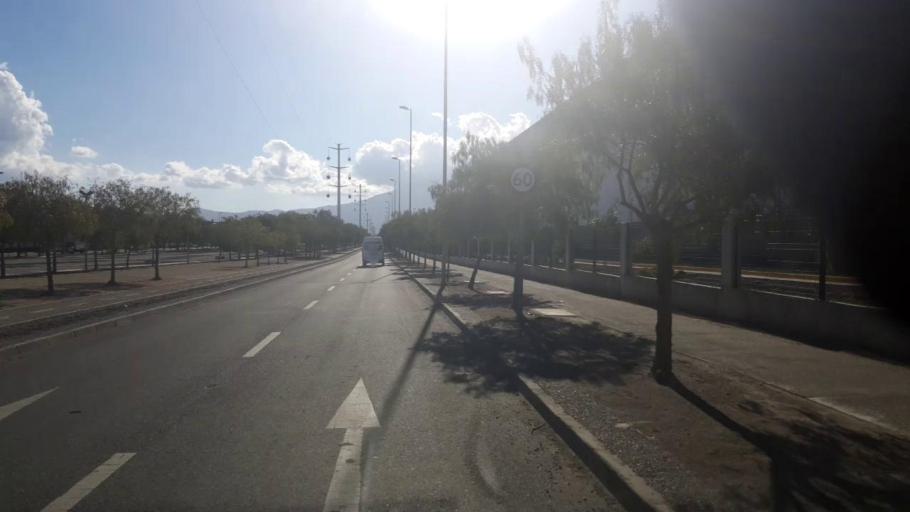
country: CL
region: Santiago Metropolitan
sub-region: Provincia de Santiago
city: Lo Prado
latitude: -33.4319
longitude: -70.7884
